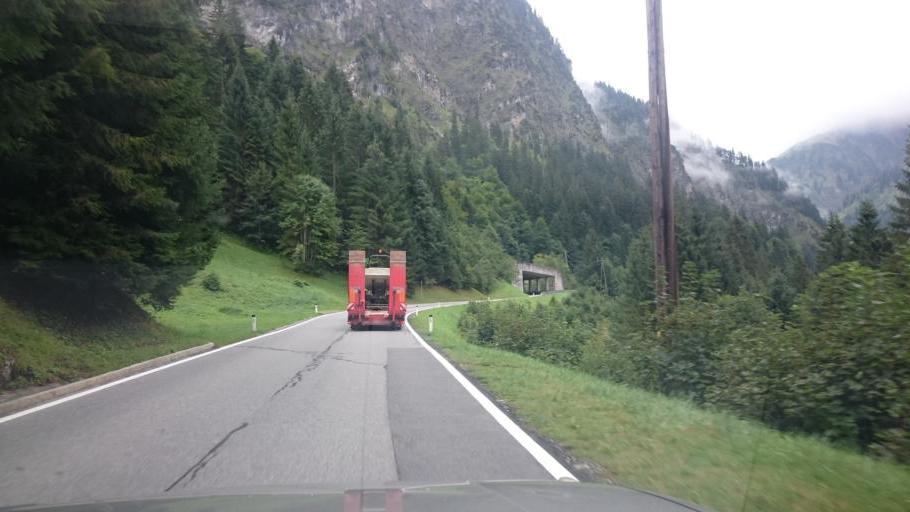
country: AT
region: Vorarlberg
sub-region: Politischer Bezirk Bregenz
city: Schroecken
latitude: 47.2778
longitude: 10.0621
